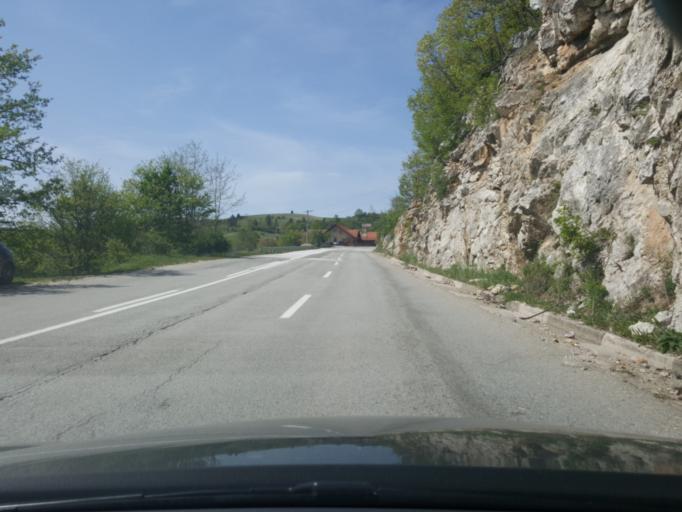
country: RS
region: Central Serbia
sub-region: Zlatiborski Okrug
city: Cajetina
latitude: 43.8029
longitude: 19.6481
